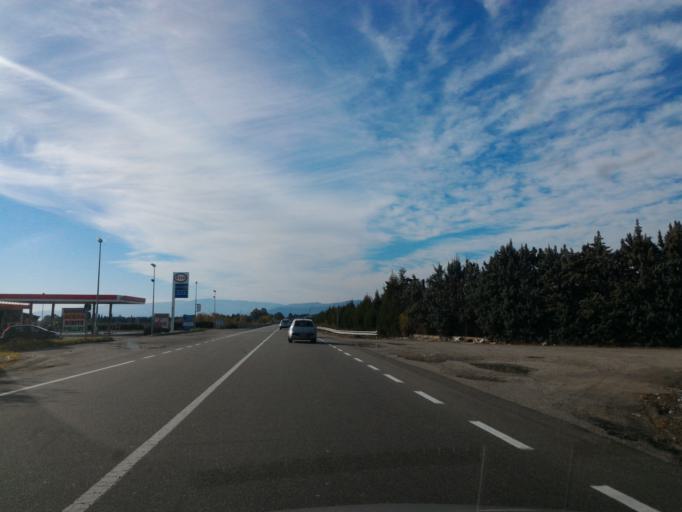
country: IT
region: Calabria
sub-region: Provincia di Catanzaro
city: Barone
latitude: 38.8665
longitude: 16.6853
